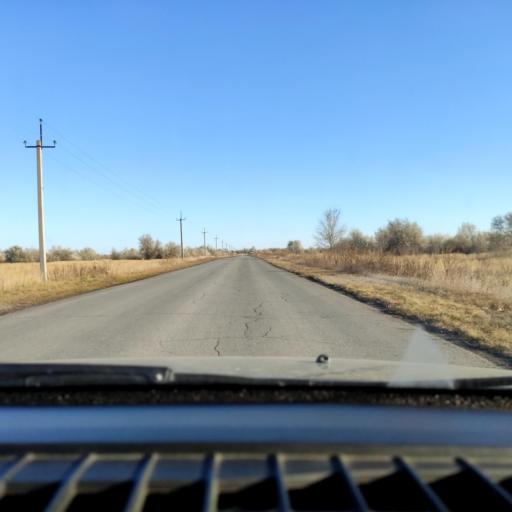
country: RU
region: Samara
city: Tol'yatti
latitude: 53.6523
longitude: 49.3250
